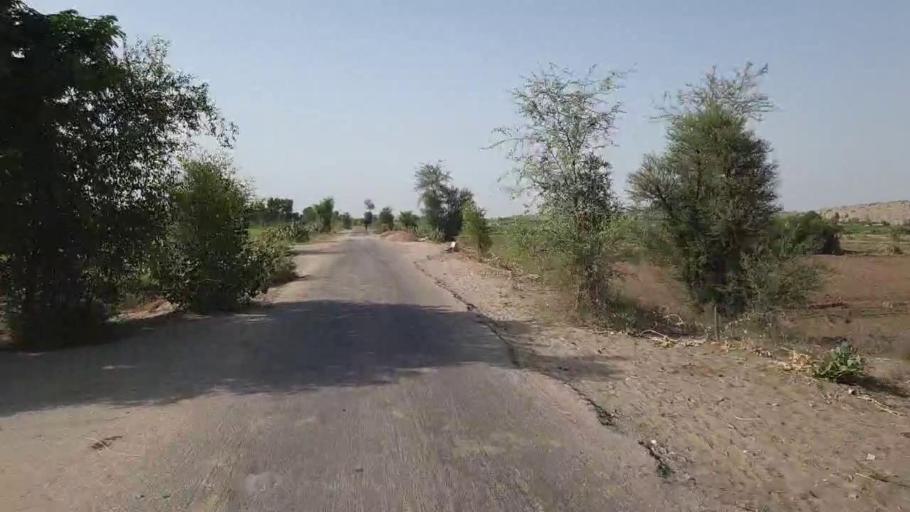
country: PK
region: Sindh
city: Kandiari
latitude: 26.6935
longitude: 68.9647
